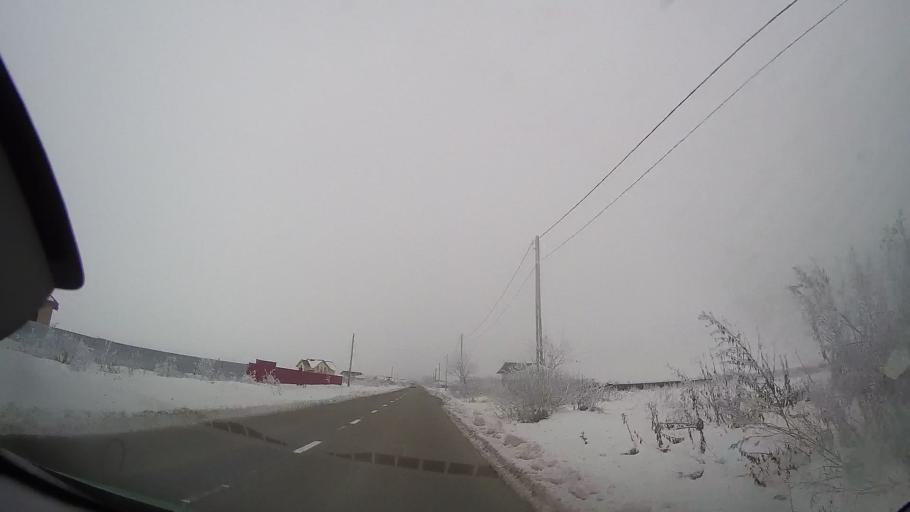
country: RO
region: Neamt
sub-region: Comuna Horia
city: Cotu Vames
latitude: 46.8918
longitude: 26.9638
